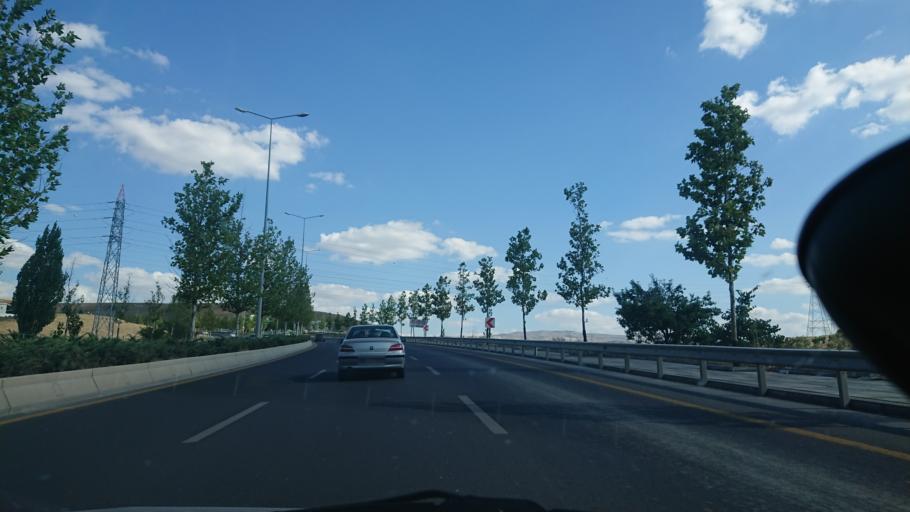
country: TR
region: Ankara
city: Mamak
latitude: 39.8859
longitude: 32.9154
